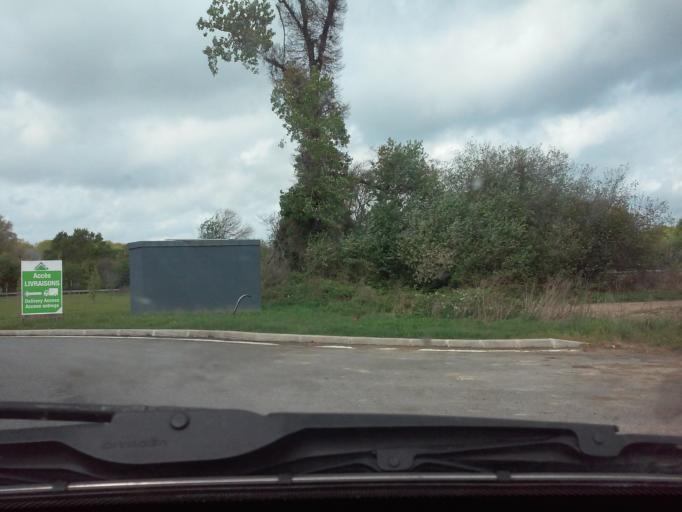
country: FR
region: Brittany
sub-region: Departement d'Ille-et-Vilaine
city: Dinard
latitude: 48.6088
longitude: -2.0698
